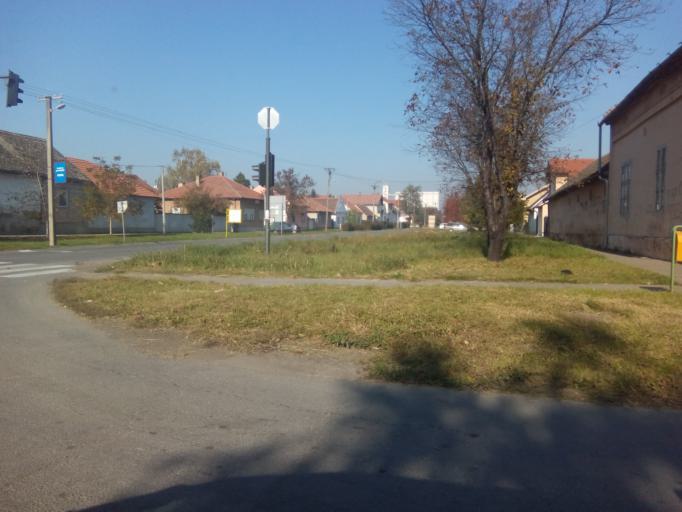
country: RS
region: Autonomna Pokrajina Vojvodina
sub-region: Juznobacki Okrug
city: Backa Palanka
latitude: 45.2525
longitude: 19.3971
